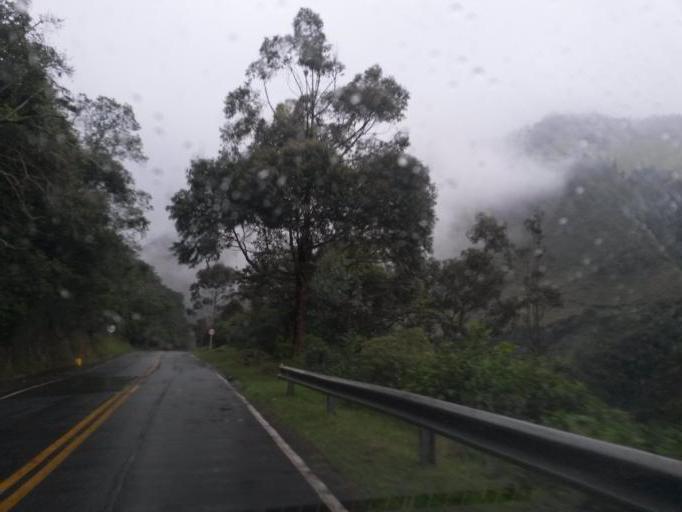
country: CO
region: Cauca
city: Popayan
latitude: 2.3779
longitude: -76.4948
